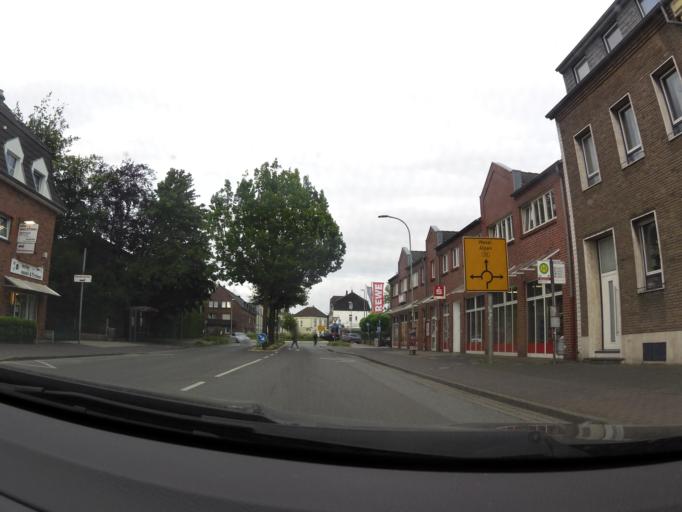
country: DE
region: North Rhine-Westphalia
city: Geldern
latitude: 51.5199
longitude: 6.3177
